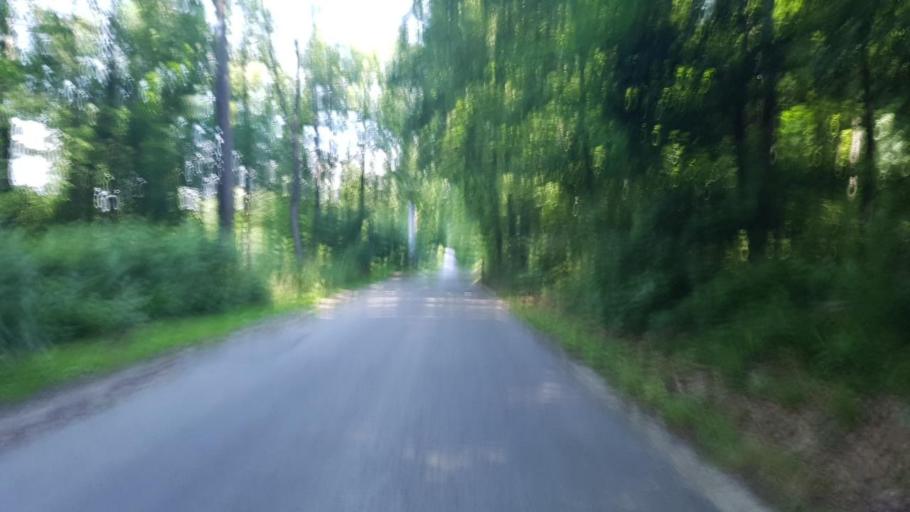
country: FR
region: Picardie
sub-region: Departement de l'Oise
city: Pont-Sainte-Maxence
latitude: 49.2810
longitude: 2.6233
